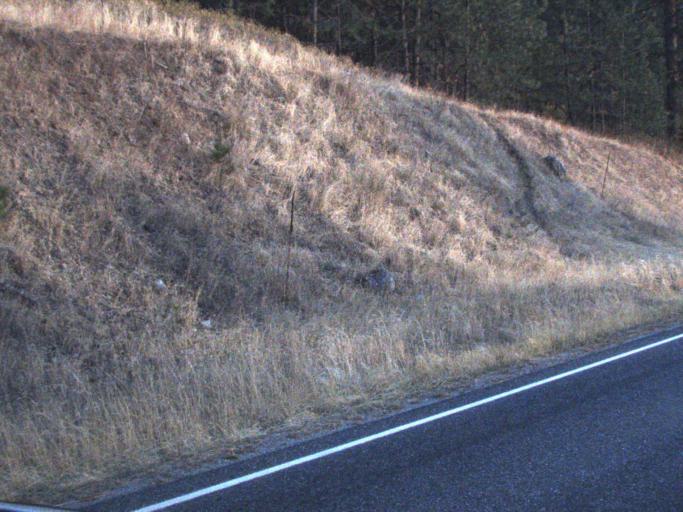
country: US
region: Washington
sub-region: Stevens County
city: Kettle Falls
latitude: 48.6934
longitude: -118.0124
